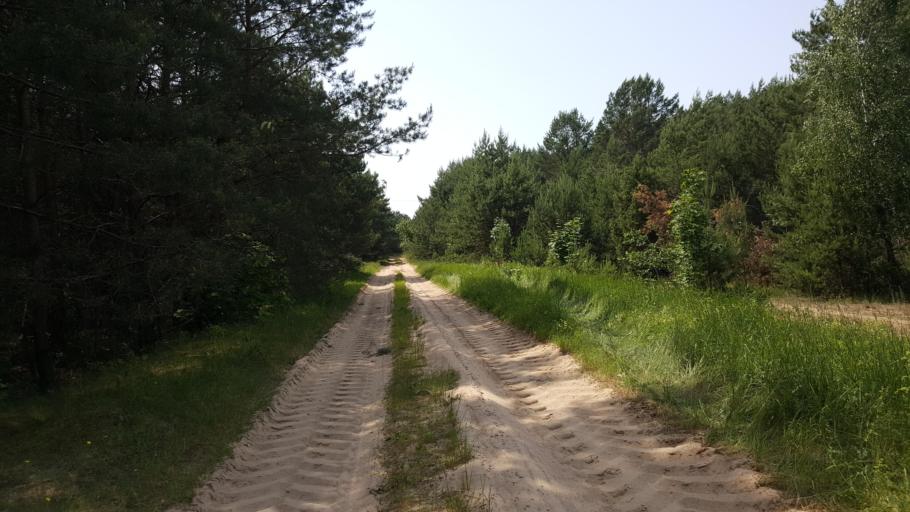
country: BY
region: Brest
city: Kamyanyuki
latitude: 52.5179
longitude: 23.8498
